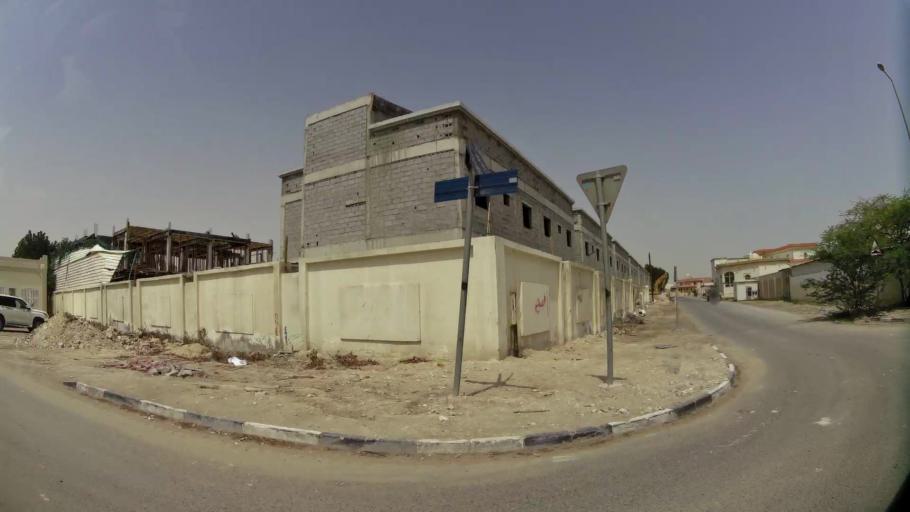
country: QA
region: Baladiyat ar Rayyan
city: Ar Rayyan
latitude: 25.2445
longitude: 51.4222
